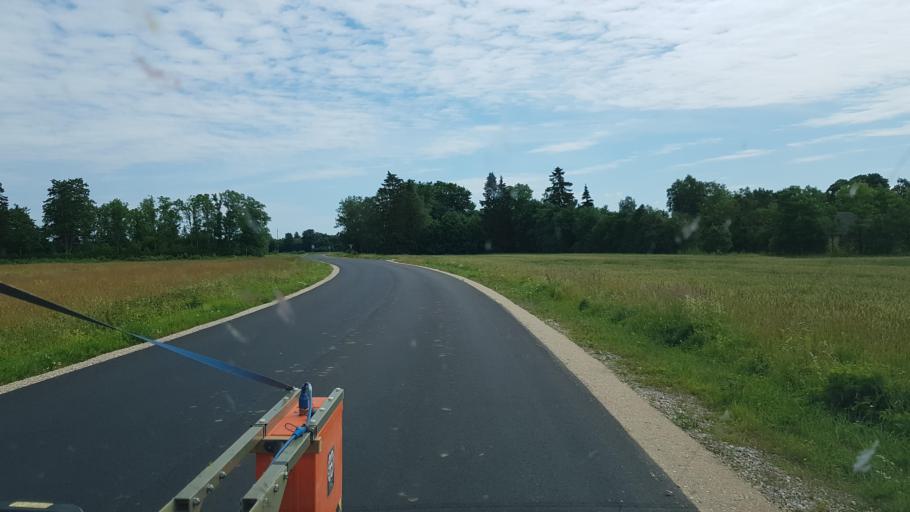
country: EE
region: Paernumaa
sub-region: Halinga vald
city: Parnu-Jaagupi
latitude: 58.6201
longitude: 24.3126
